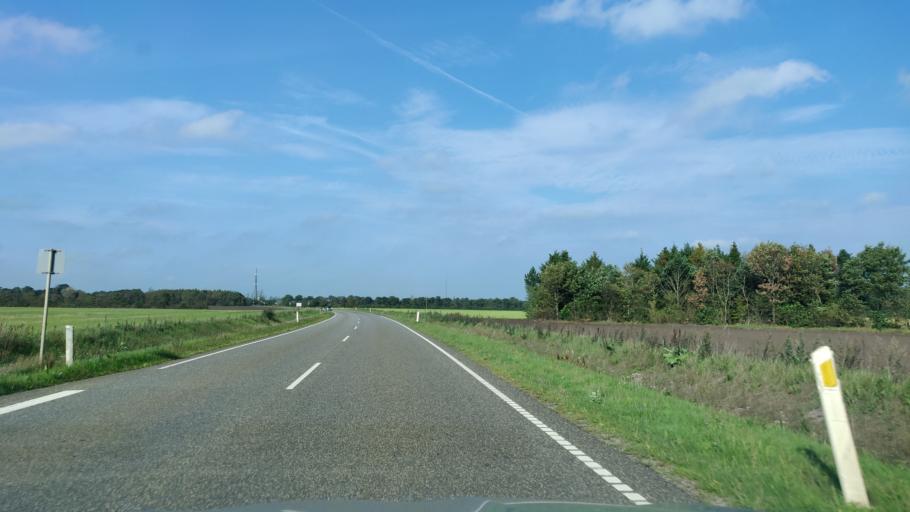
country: DK
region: Central Jutland
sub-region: Herning Kommune
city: Sunds
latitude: 56.2655
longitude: 9.0147
